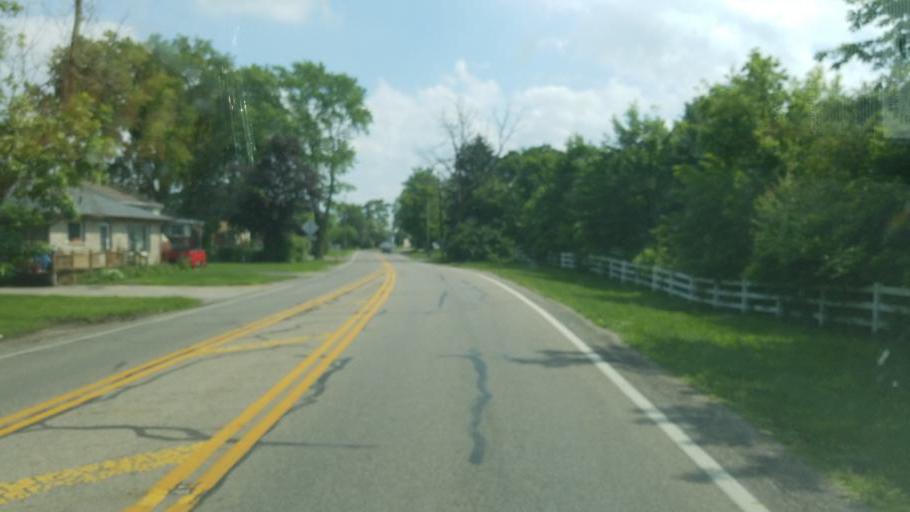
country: US
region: Ohio
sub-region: Franklin County
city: Lincoln Village
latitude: 39.9546
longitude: -83.1459
